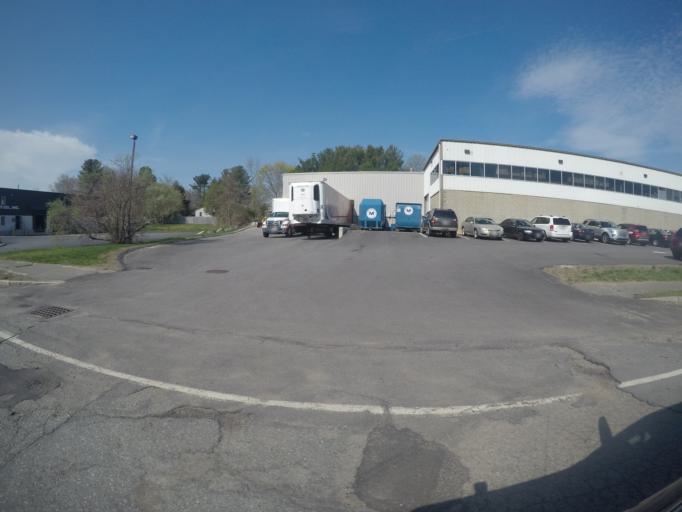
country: US
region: Massachusetts
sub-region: Bristol County
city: Easton
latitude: 42.0456
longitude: -71.0769
